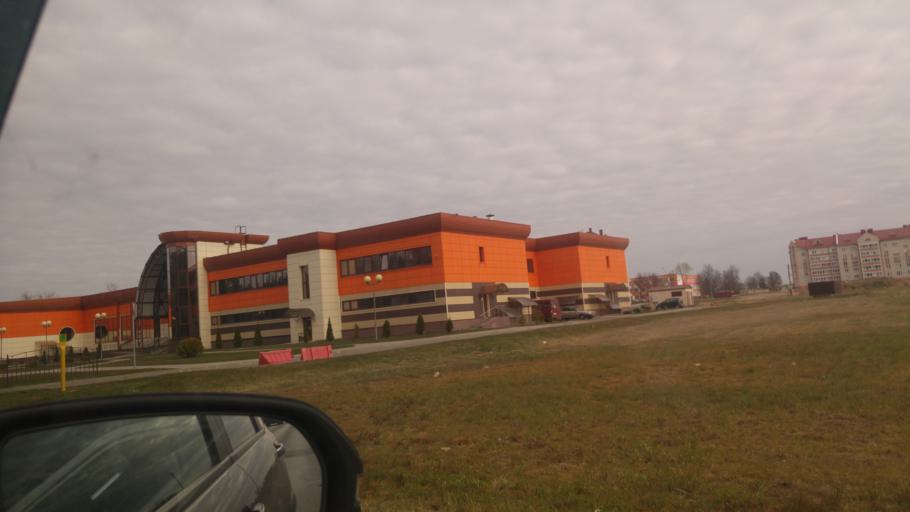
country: BY
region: Minsk
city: Chervyen'
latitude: 53.6993
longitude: 28.4190
